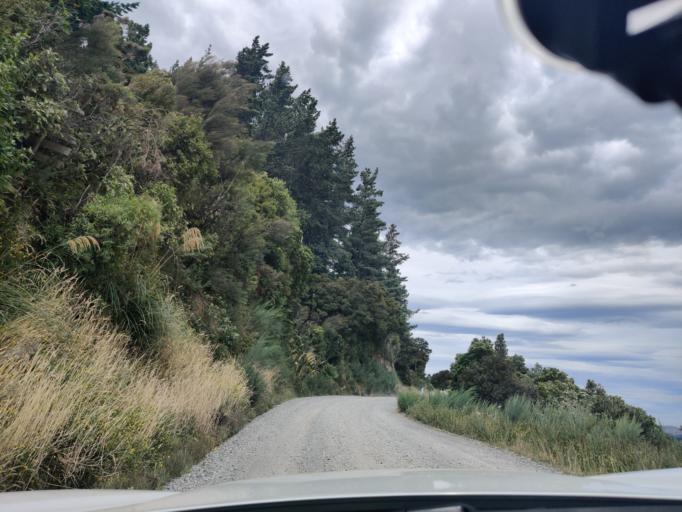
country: NZ
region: Wellington
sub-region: Masterton District
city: Masterton
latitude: -41.0406
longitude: 175.4040
